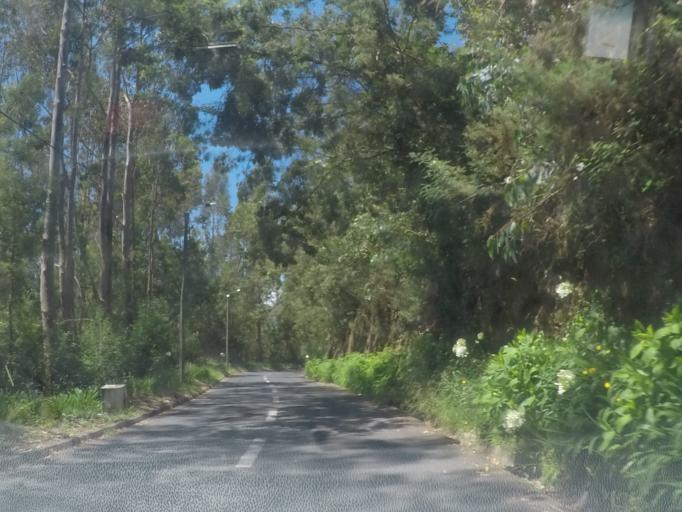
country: PT
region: Madeira
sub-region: Camara de Lobos
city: Curral das Freiras
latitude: 32.6876
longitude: -16.9775
